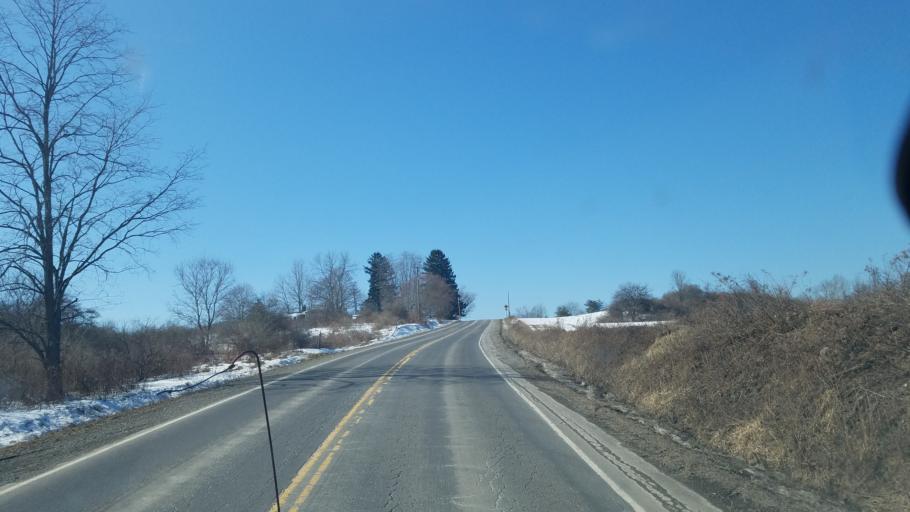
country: US
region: New York
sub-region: Steuben County
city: Hornell
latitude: 42.3629
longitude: -77.6916
